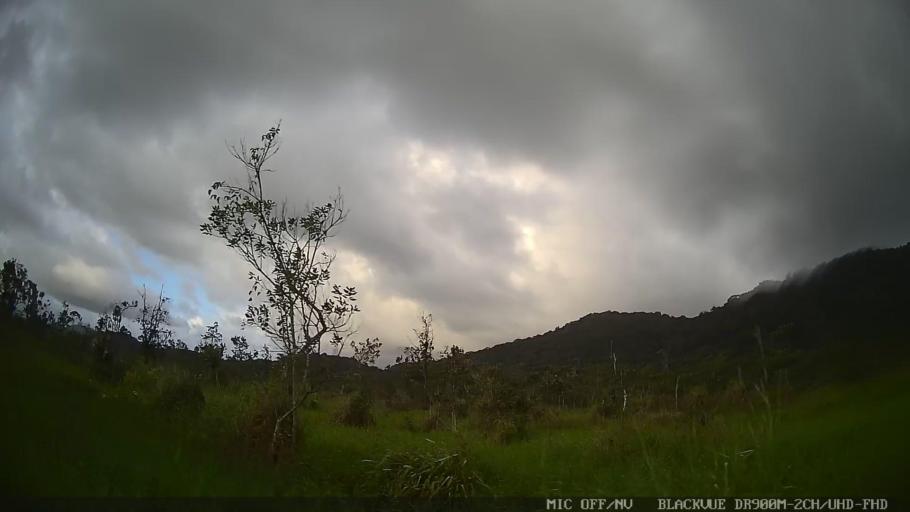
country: BR
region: Sao Paulo
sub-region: Itanhaem
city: Itanhaem
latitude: -24.1376
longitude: -46.7773
